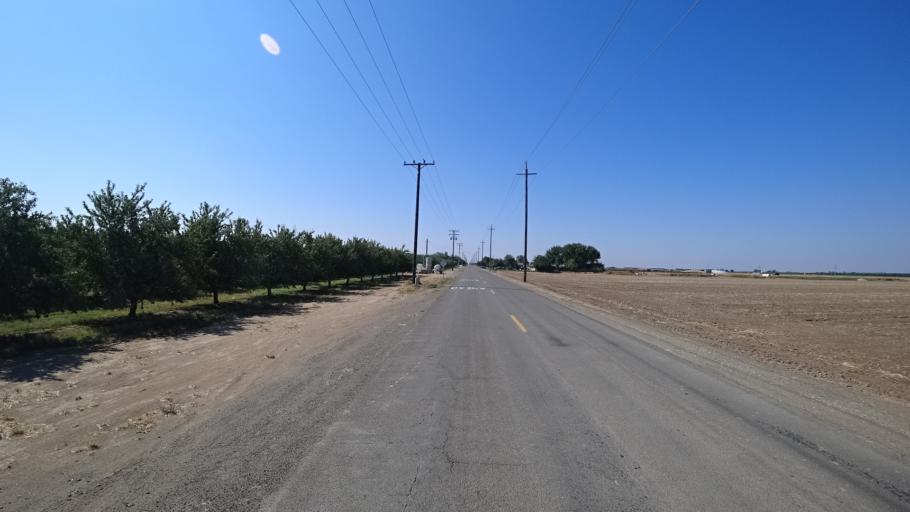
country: US
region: California
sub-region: Kings County
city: Hanford
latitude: 36.3708
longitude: -119.5830
